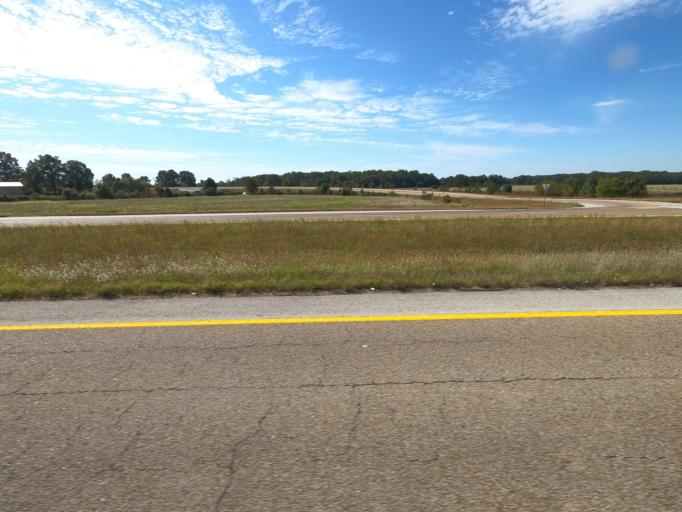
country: US
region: Tennessee
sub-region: Crockett County
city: Alamo
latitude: 35.8191
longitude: -89.1671
